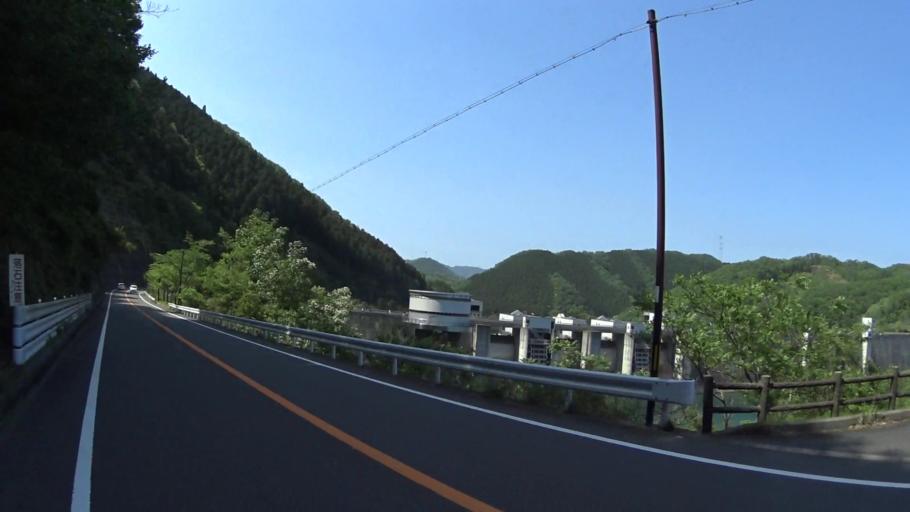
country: JP
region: Kyoto
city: Kameoka
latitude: 35.1468
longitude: 135.5158
